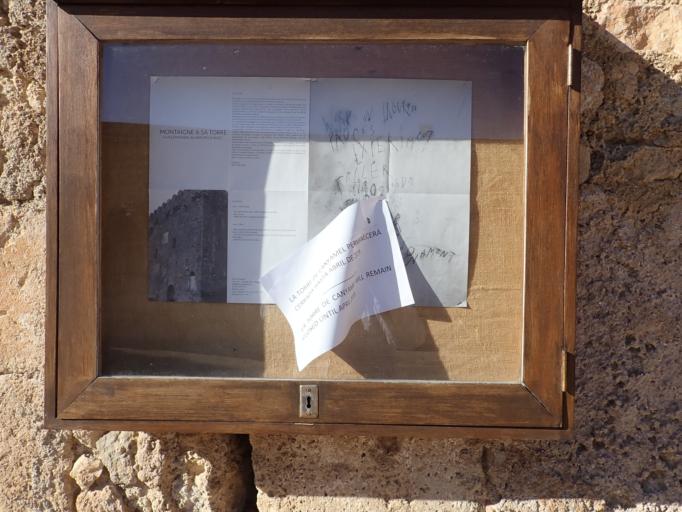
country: ES
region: Balearic Islands
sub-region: Illes Balears
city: Capdepera
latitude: 39.6675
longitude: 3.4118
